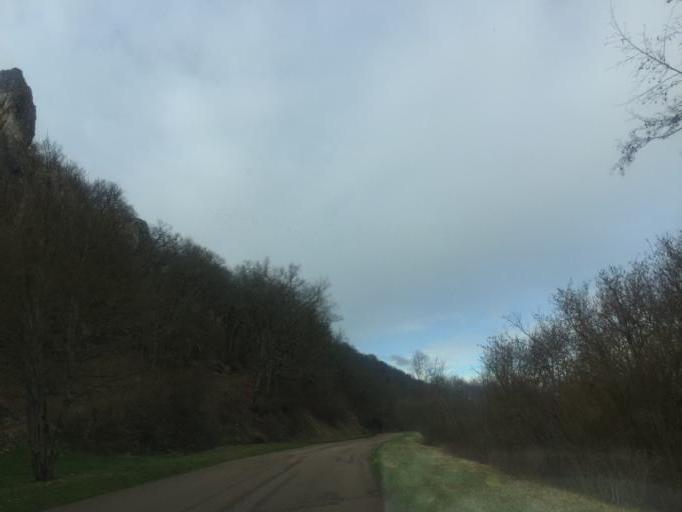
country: FR
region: Bourgogne
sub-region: Departement de la Nievre
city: Clamecy
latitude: 47.4930
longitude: 3.5072
